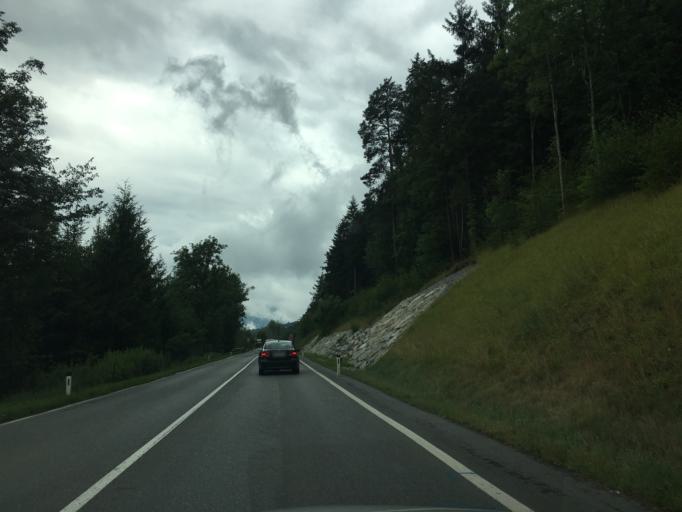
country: AT
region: Tyrol
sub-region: Politischer Bezirk Imst
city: Imst
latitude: 47.2542
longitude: 10.7498
